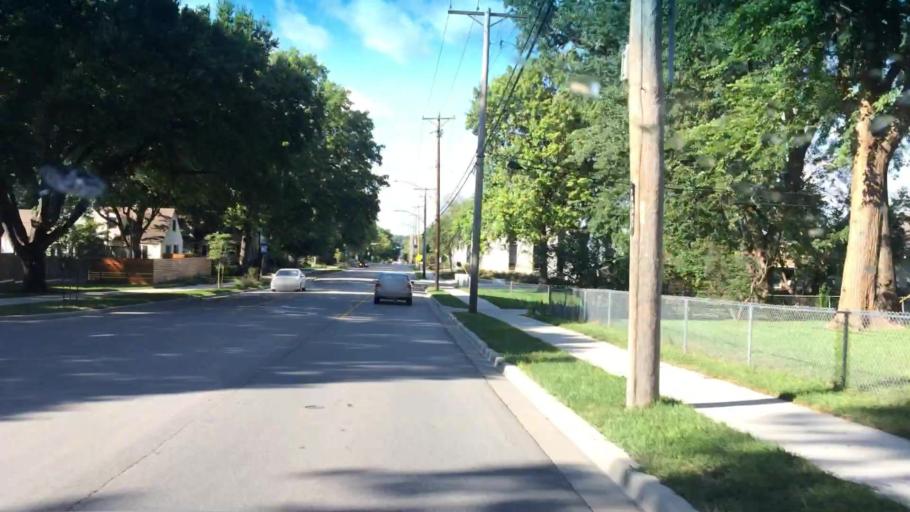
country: US
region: Kansas
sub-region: Johnson County
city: Prairie Village
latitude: 38.9948
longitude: -94.6304
